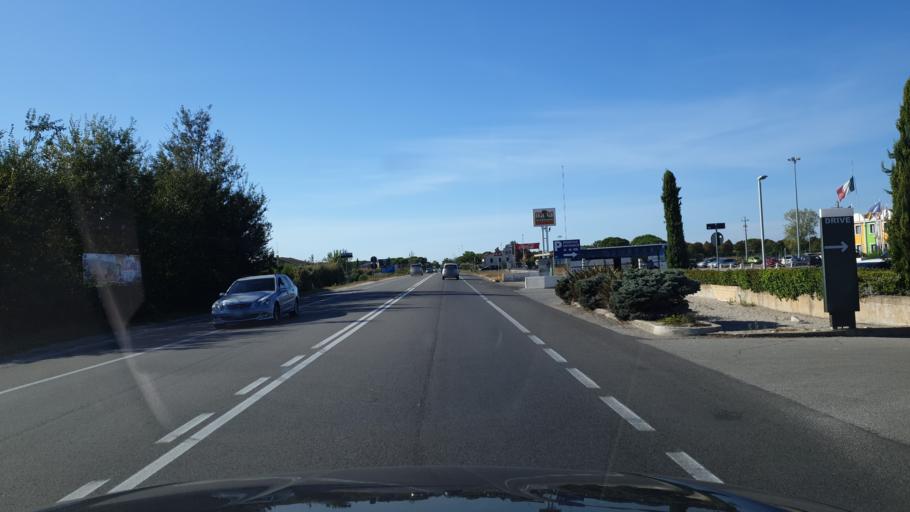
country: IT
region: Emilia-Romagna
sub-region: Provincia di Rimini
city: Santa Giustina
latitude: 44.0892
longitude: 12.5139
